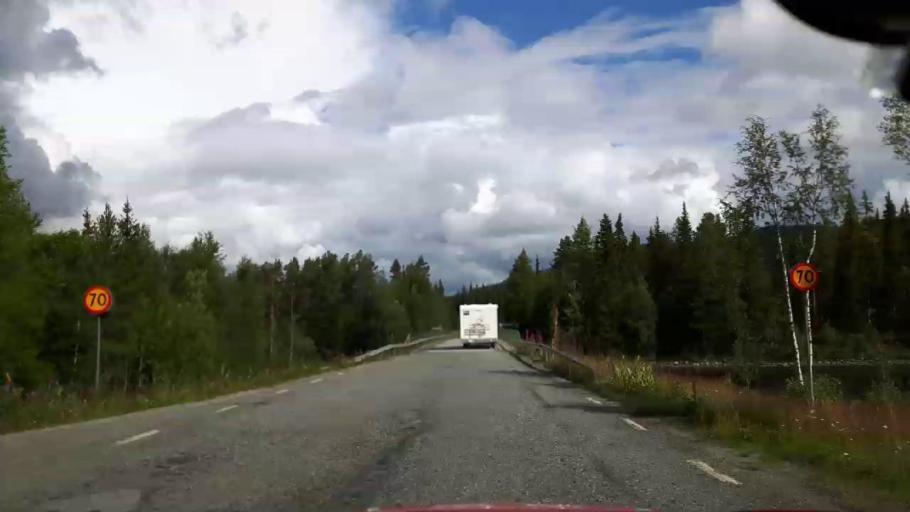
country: SE
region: Vaesterbotten
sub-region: Vilhelmina Kommun
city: Sjoberg
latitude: 64.9359
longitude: 15.8579
